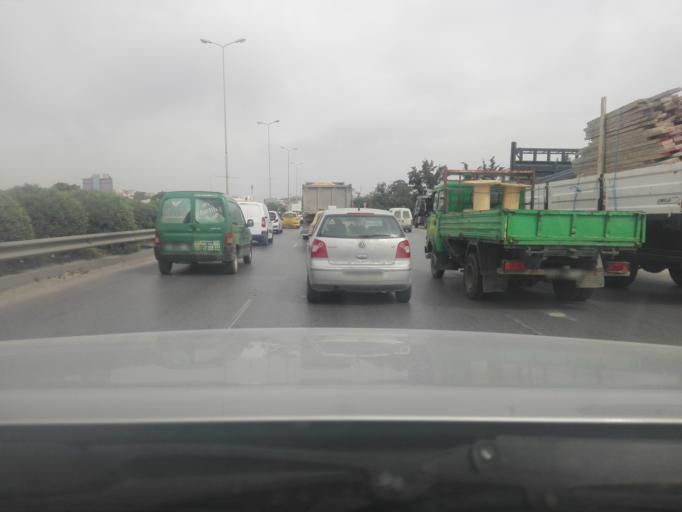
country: TN
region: Bin 'Arus
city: Ben Arous
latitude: 36.7567
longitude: 10.2011
